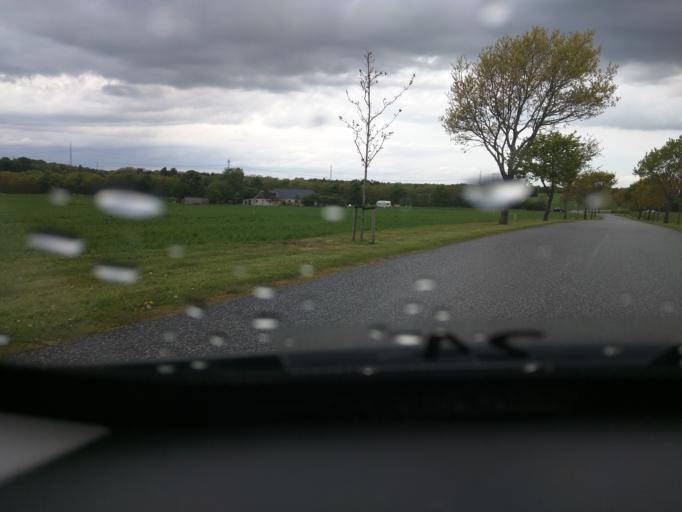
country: DK
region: Central Jutland
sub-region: Viborg Kommune
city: Bjerringbro
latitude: 56.4897
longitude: 9.5771
